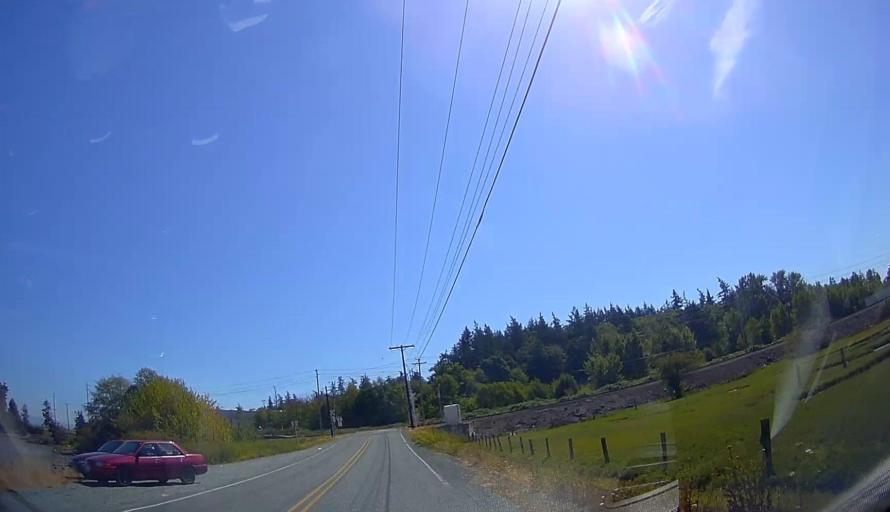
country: US
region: Washington
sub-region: Skagit County
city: Anacortes
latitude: 48.4664
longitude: -122.5376
